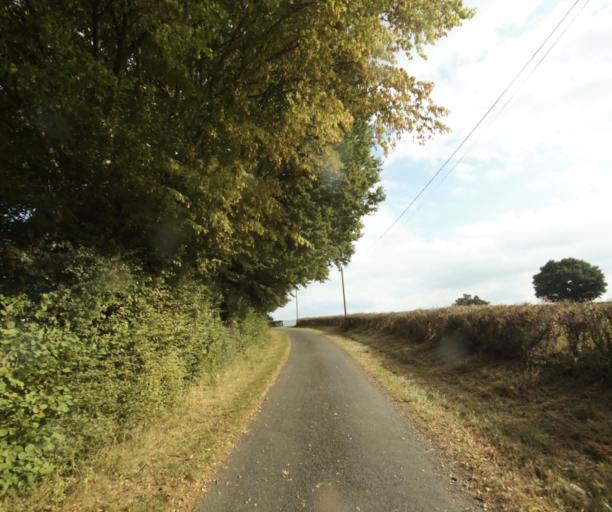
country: FR
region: Bourgogne
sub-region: Departement de Saone-et-Loire
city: Palinges
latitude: 46.5069
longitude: 4.2506
